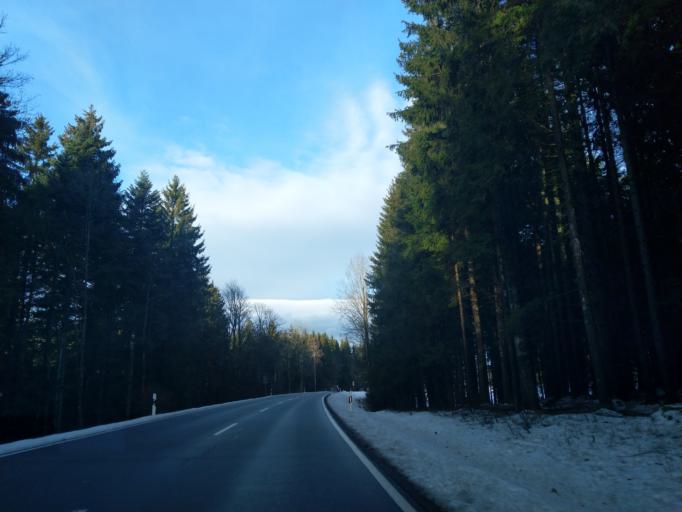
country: DE
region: Bavaria
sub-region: Lower Bavaria
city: Bischofsmais
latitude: 48.8935
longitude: 13.0909
